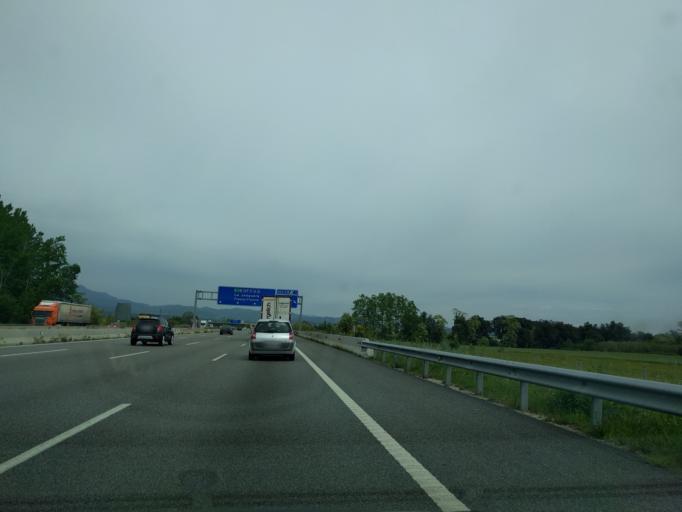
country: ES
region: Catalonia
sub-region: Provincia de Girona
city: Vilablareix
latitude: 41.9499
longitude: 2.7881
